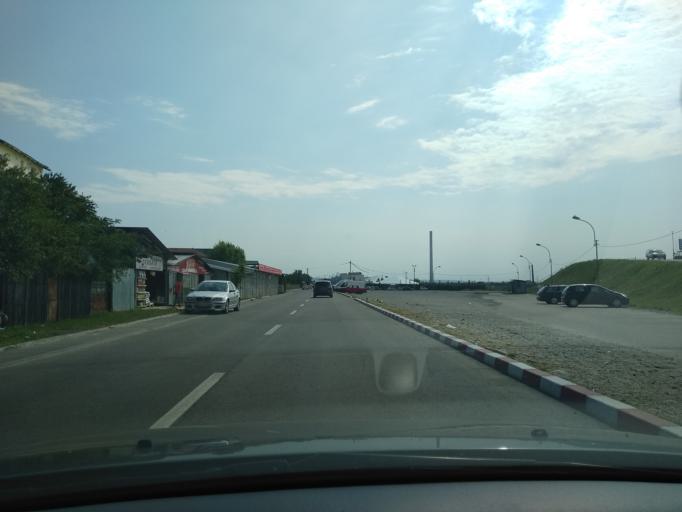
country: RO
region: Gorj
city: Targu Jiu
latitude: 45.0338
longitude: 23.2660
